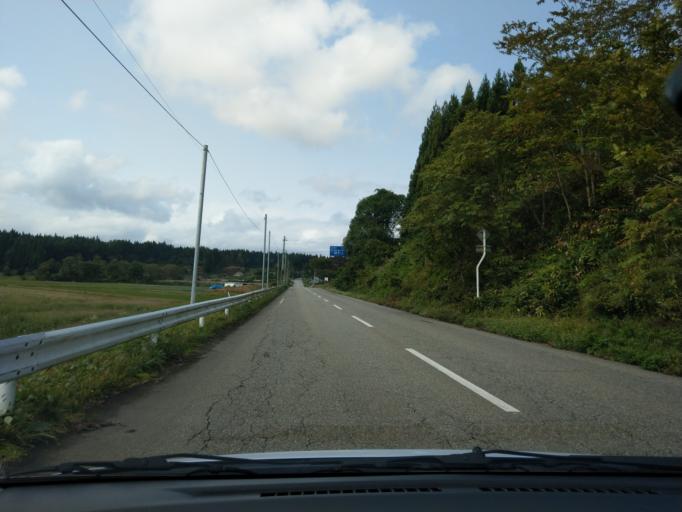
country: JP
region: Akita
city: Omagari
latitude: 39.5191
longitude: 140.3042
